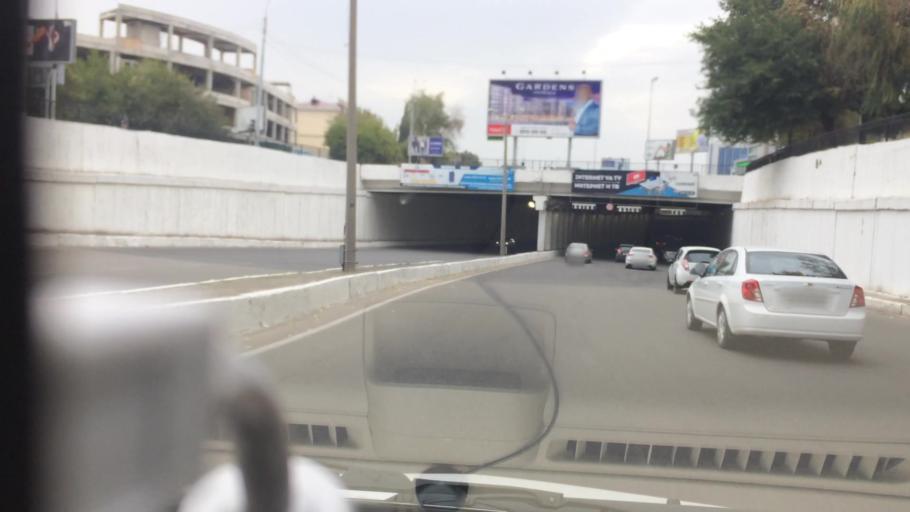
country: UZ
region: Toshkent Shahri
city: Tashkent
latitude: 41.2906
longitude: 69.2835
